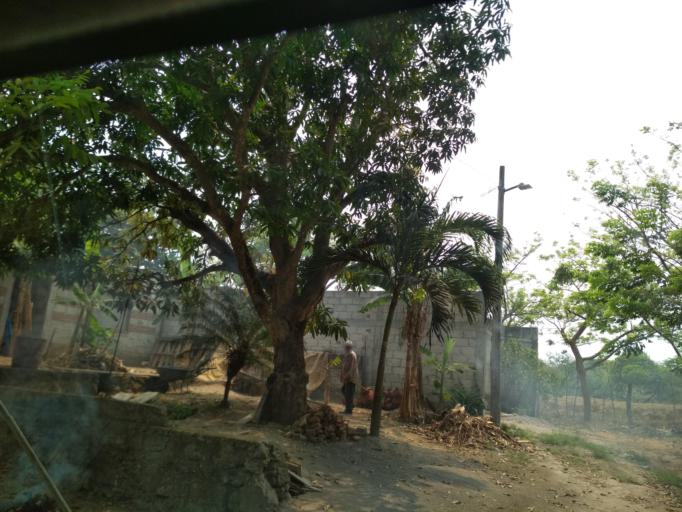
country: MX
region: Veracruz
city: El Tejar
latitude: 19.0707
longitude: -96.1542
